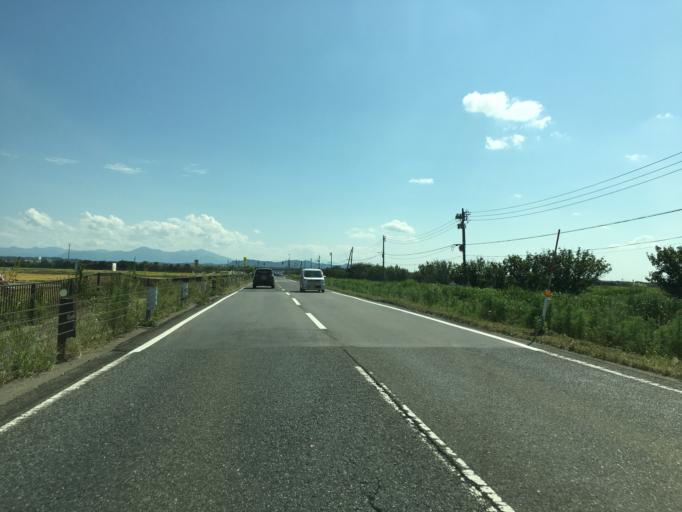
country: JP
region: Niigata
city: Niitsu-honcho
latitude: 37.8275
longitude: 139.0978
